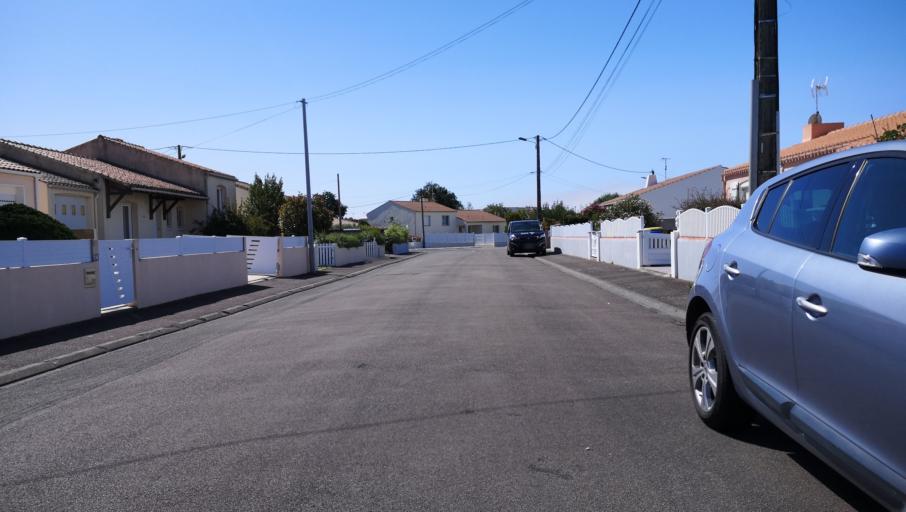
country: FR
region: Pays de la Loire
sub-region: Departement de la Vendee
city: Chateau-d'Olonne
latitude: 46.5017
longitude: -1.7563
